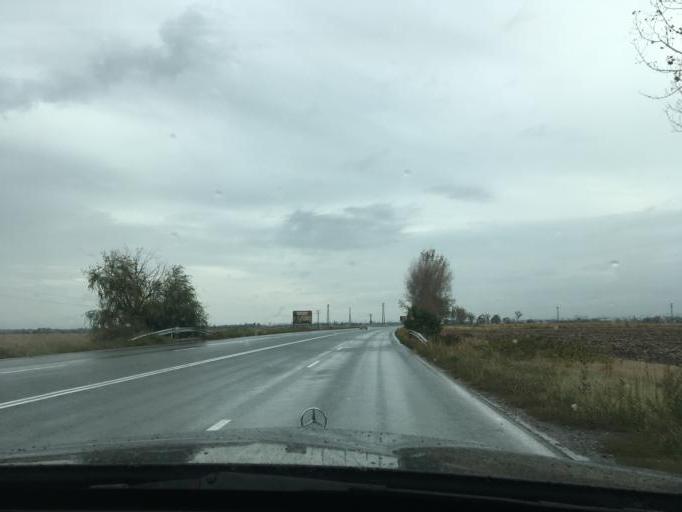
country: BG
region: Sofiya
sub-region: Obshtina Bozhurishte
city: Bozhurishte
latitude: 42.7669
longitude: 23.2105
